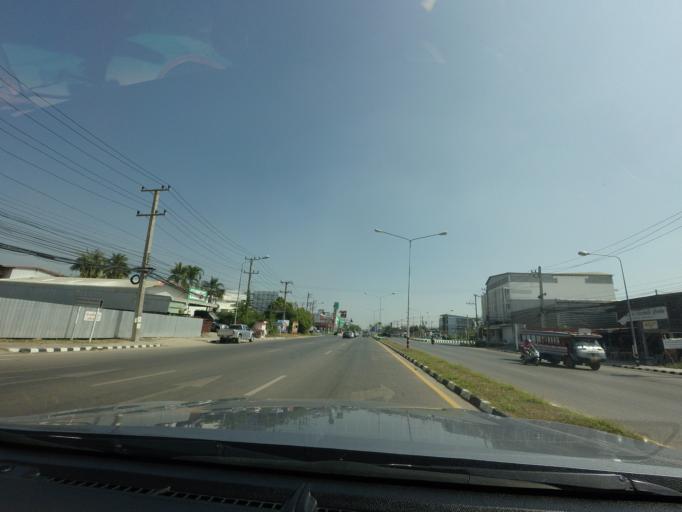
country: TH
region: Sukhothai
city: Sukhothai
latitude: 17.0094
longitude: 99.8041
